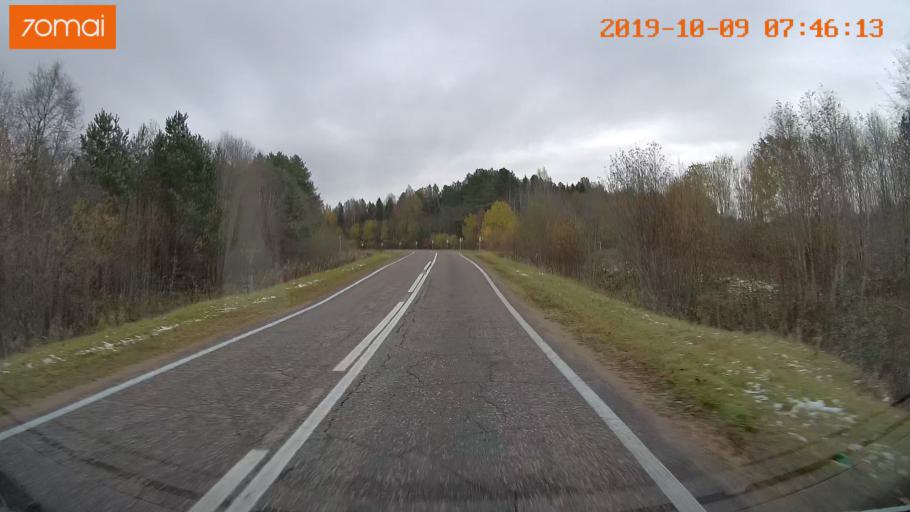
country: RU
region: Jaroslavl
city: Kukoboy
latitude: 58.6557
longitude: 39.7833
